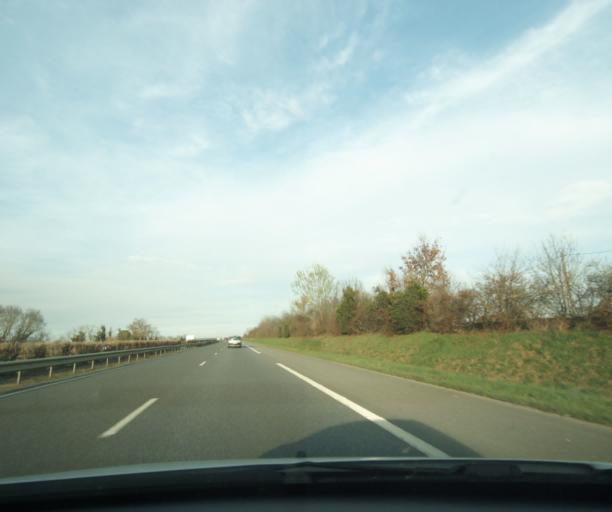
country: FR
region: Midi-Pyrenees
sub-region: Departement de la Haute-Garonne
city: Rieux-Volvestre
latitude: 43.2780
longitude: 1.1457
